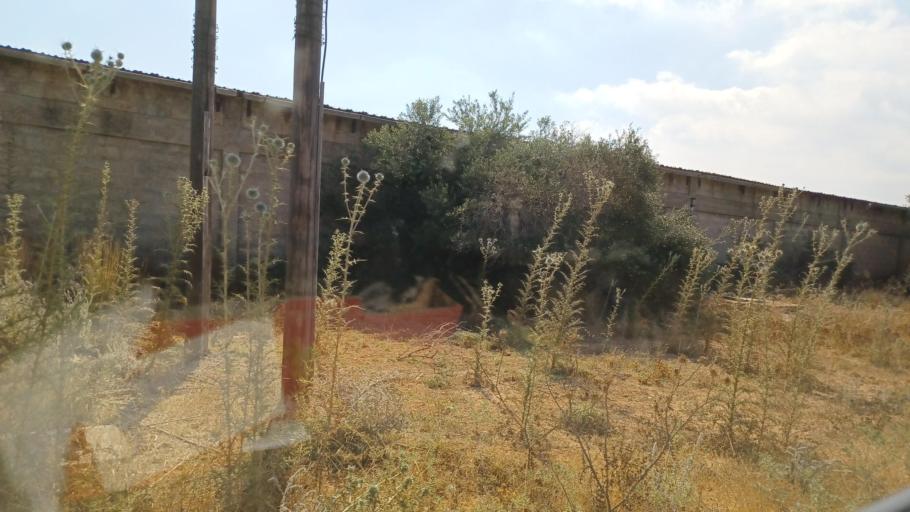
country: CY
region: Ammochostos
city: Deryneia
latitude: 35.0710
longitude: 33.9545
